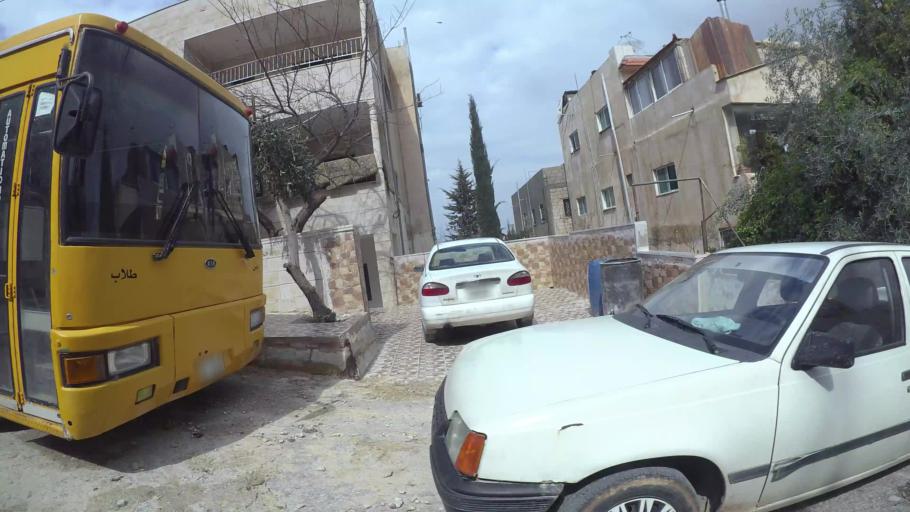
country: JO
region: Amman
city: Al Jubayhah
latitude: 32.0342
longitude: 35.8262
